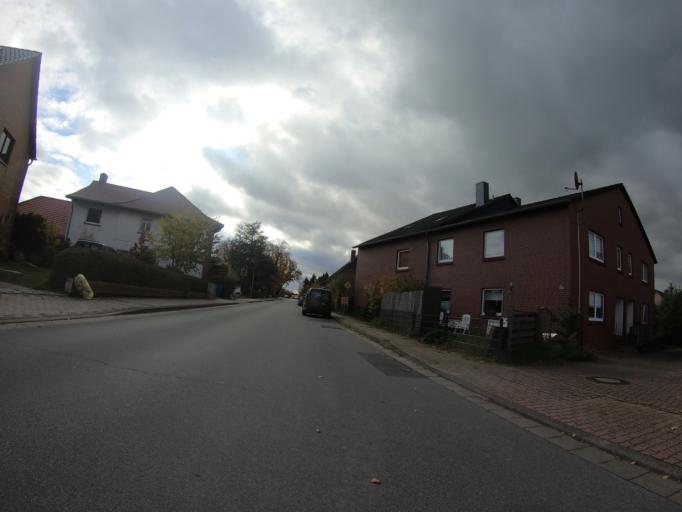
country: DE
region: Lower Saxony
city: Ribbesbuttel
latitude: 52.4278
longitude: 10.4853
